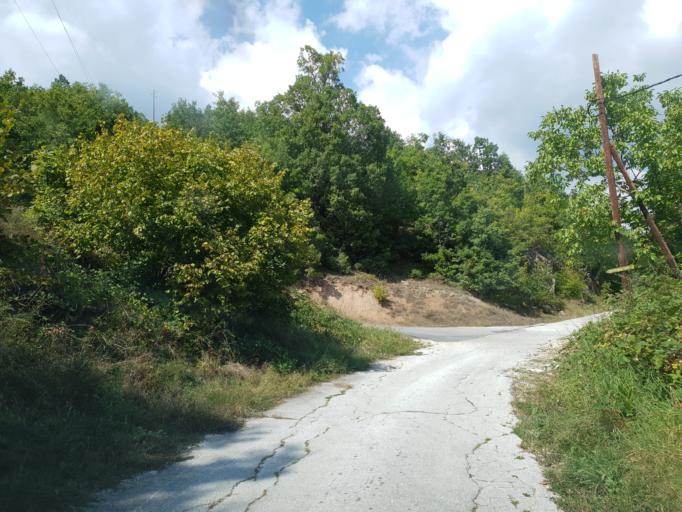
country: MK
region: Makedonski Brod
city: Samokov
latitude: 41.7449
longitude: 21.1050
